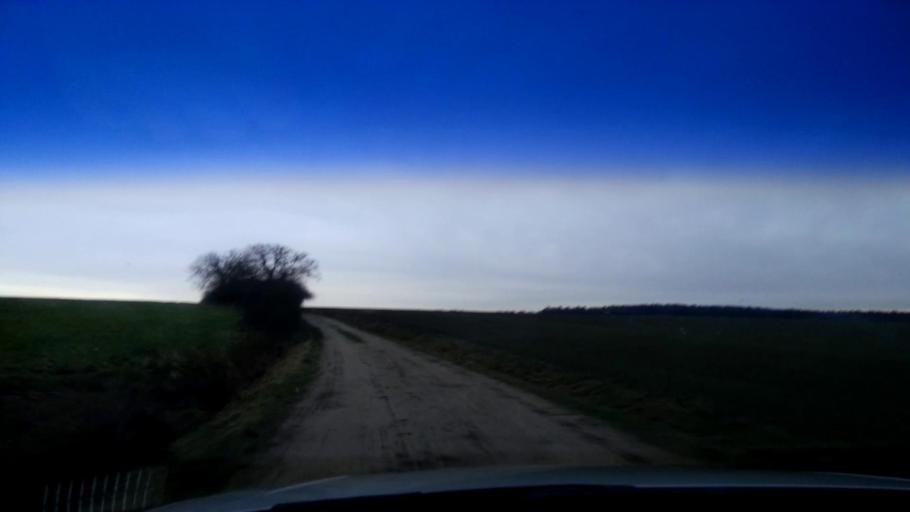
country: DE
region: Bavaria
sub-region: Upper Franconia
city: Litzendorf
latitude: 49.9185
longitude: 10.9887
